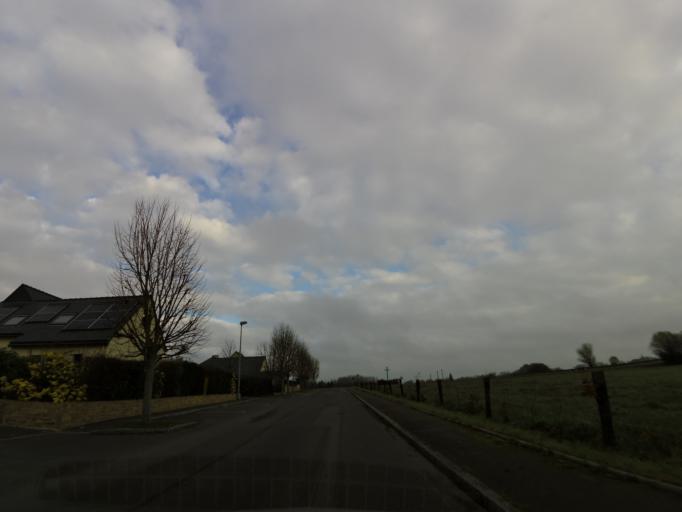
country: FR
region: Brittany
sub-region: Departement d'Ille-et-Vilaine
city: Orgeres
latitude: 47.9915
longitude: -1.6638
